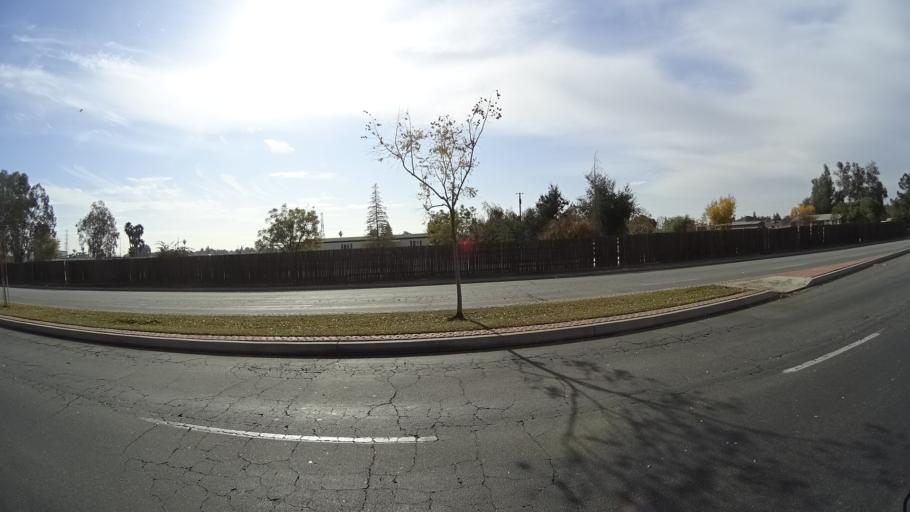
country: US
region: California
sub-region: Kern County
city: Greenacres
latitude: 35.4017
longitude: -119.0707
